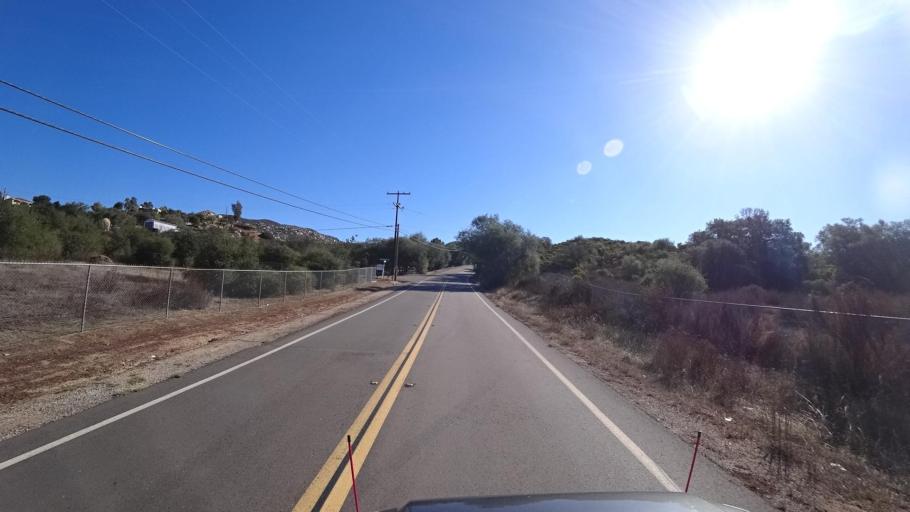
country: US
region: California
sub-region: San Diego County
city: Jamul
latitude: 32.6781
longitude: -116.7490
